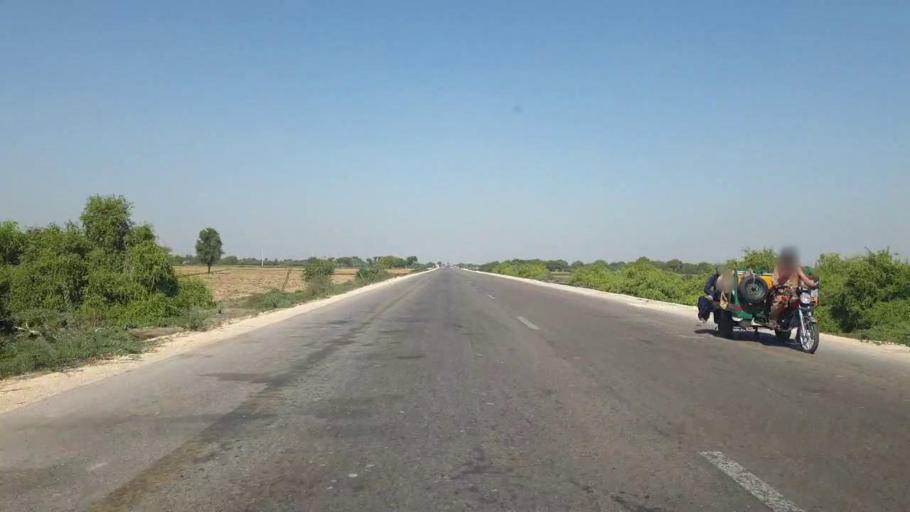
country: PK
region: Sindh
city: Talhar
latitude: 24.8213
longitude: 68.8159
